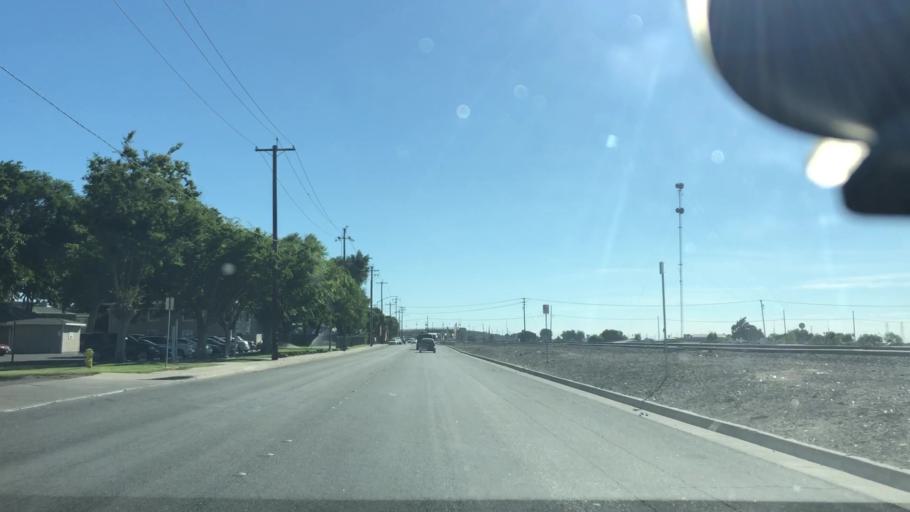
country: US
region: California
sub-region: San Joaquin County
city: Tracy
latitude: 37.7361
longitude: -121.4200
